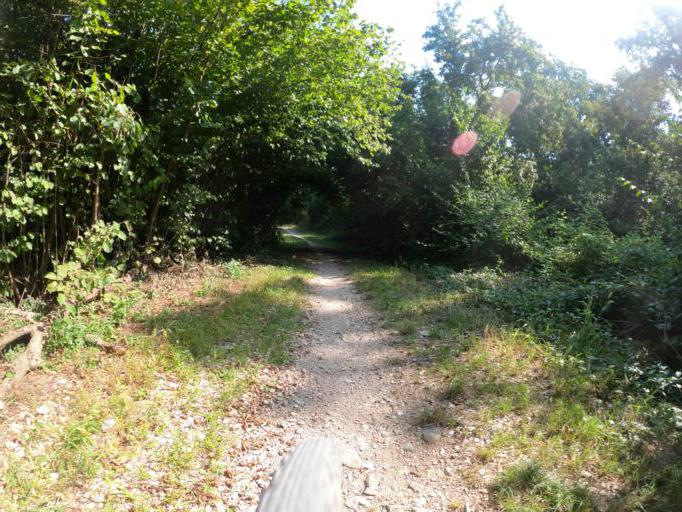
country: IT
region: Veneto
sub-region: Provincia di Verona
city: Caprino Veronese
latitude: 45.5836
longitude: 10.7819
